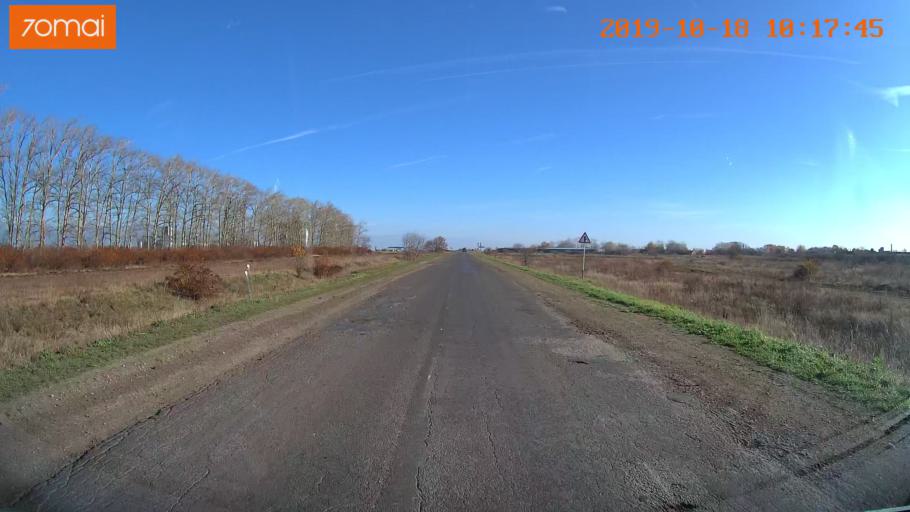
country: RU
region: Tula
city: Kurkino
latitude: 53.4140
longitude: 38.6244
